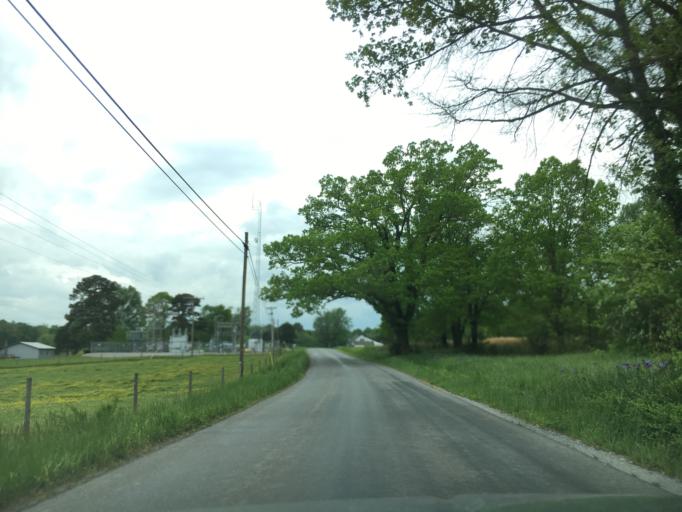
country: US
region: Virginia
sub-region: Campbell County
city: Rustburg
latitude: 37.1669
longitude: -79.0579
